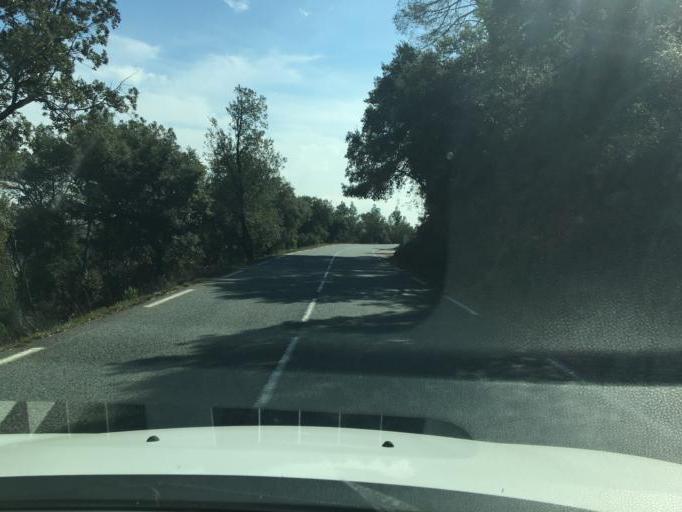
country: FR
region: Provence-Alpes-Cote d'Azur
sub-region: Departement du Var
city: Bargemon
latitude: 43.6106
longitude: 6.5512
